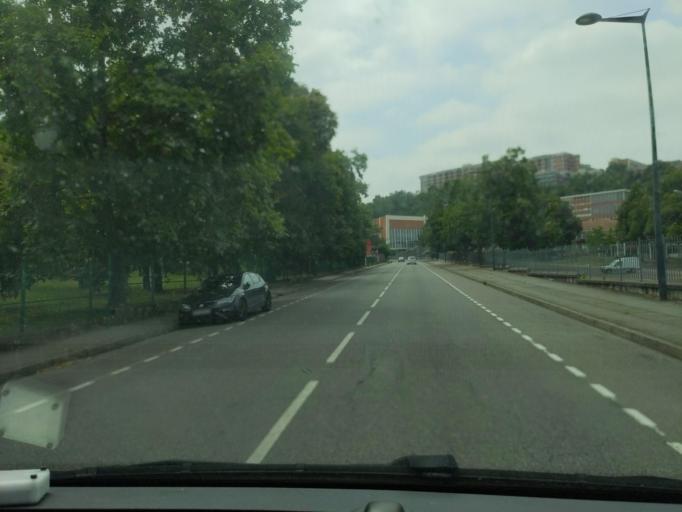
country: FR
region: Midi-Pyrenees
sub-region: Departement de la Haute-Garonne
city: Ramonville-Saint-Agne
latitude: 43.5626
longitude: 1.4599
